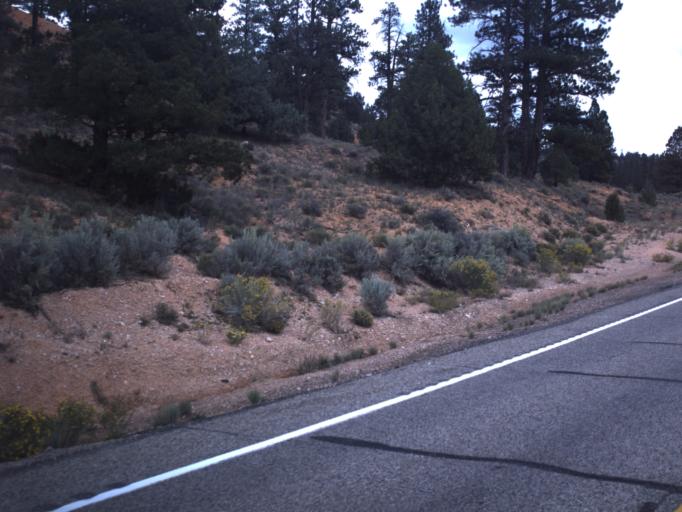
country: US
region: Utah
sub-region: Garfield County
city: Panguitch
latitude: 37.7298
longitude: -112.2759
